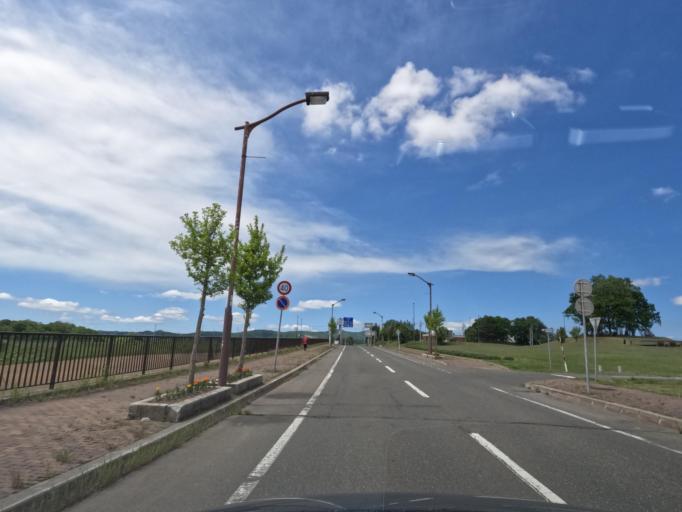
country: JP
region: Hokkaido
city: Shimo-furano
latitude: 43.4618
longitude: 142.4597
